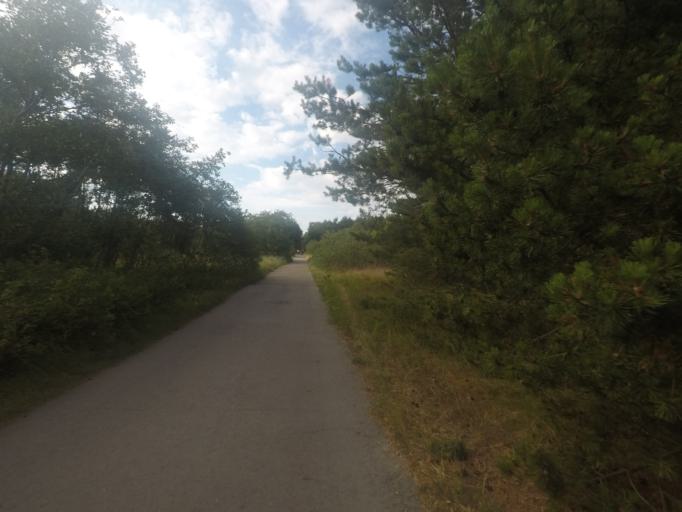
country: LT
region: Klaipedos apskritis
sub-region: Klaipeda
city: Klaipeda
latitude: 55.6850
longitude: 21.1040
